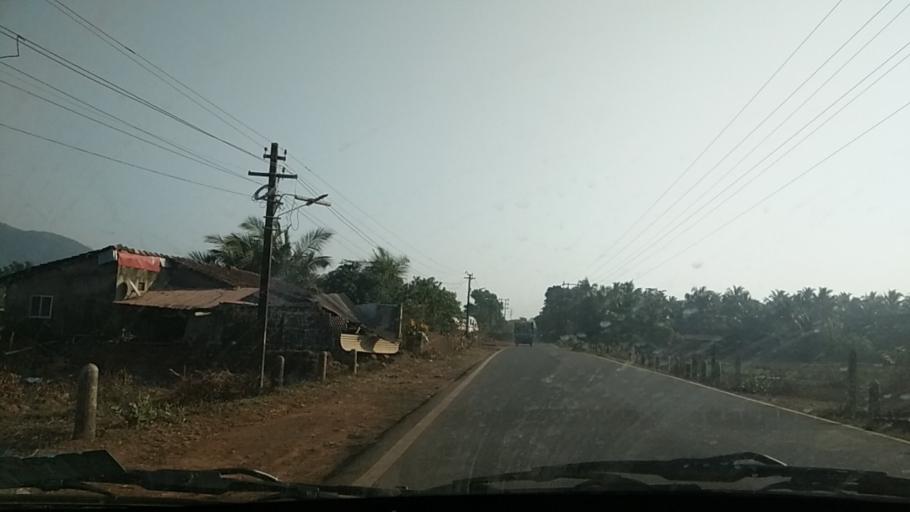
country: IN
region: Goa
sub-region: South Goa
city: Cuncolim
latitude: 15.1869
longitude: 74.0234
